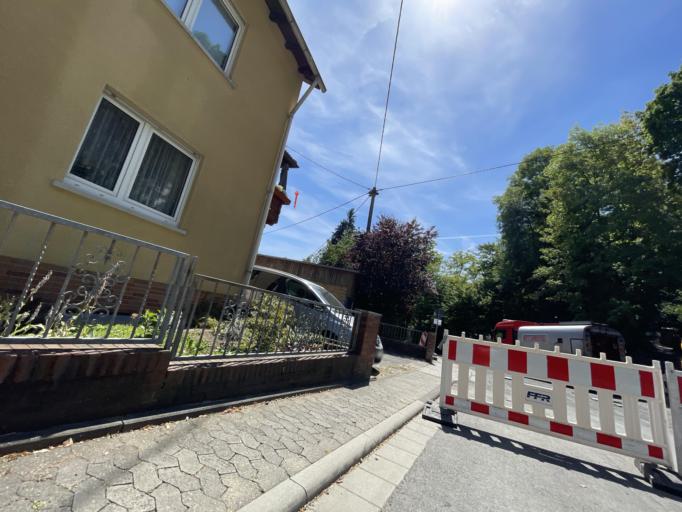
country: GB
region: England
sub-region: East Sussex
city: Eastbourne
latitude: 50.5921
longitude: 0.4534
